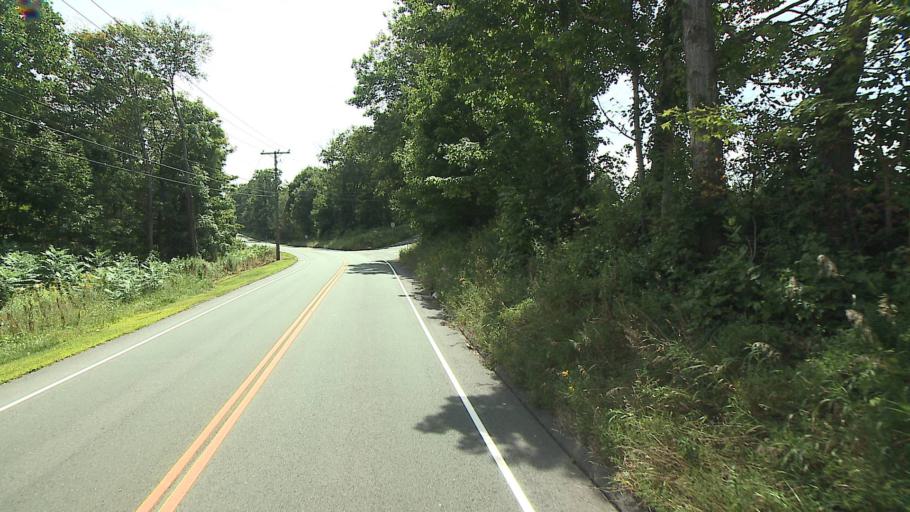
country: US
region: Connecticut
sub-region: Litchfield County
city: Bethlehem Village
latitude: 41.6163
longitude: -73.1969
